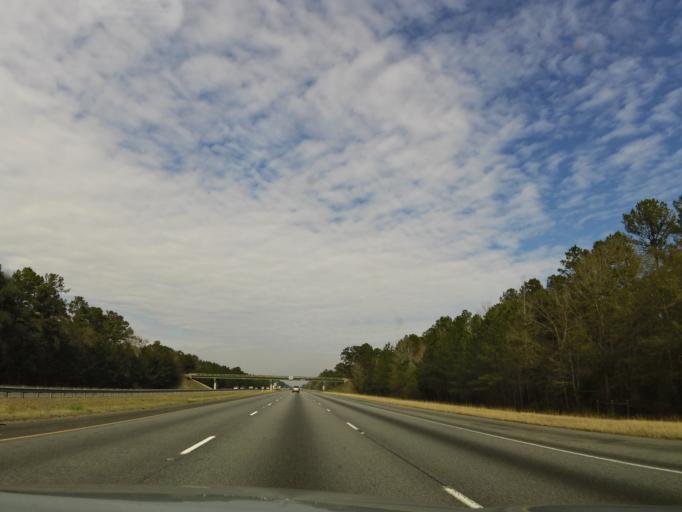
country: US
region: Georgia
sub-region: McIntosh County
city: Darien
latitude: 31.5782
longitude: -81.4324
